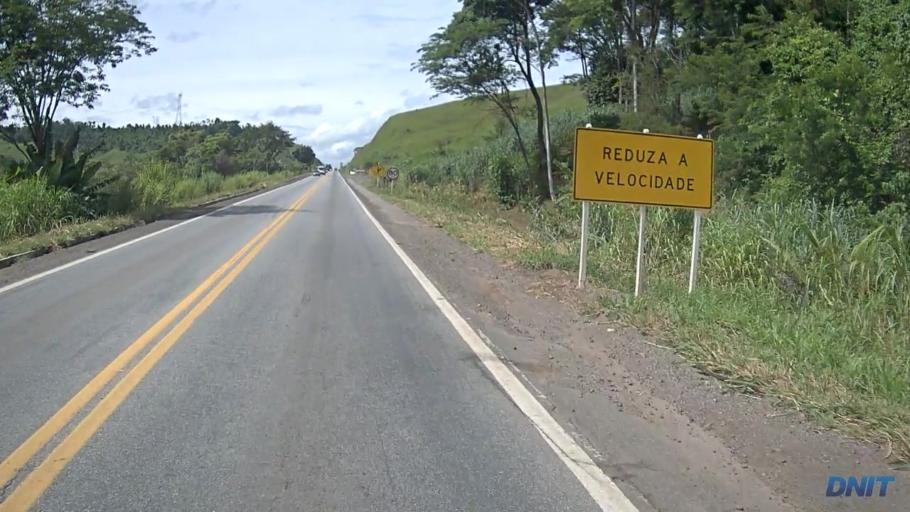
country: BR
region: Minas Gerais
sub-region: Ipatinga
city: Ipatinga
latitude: -19.4229
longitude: -42.4954
